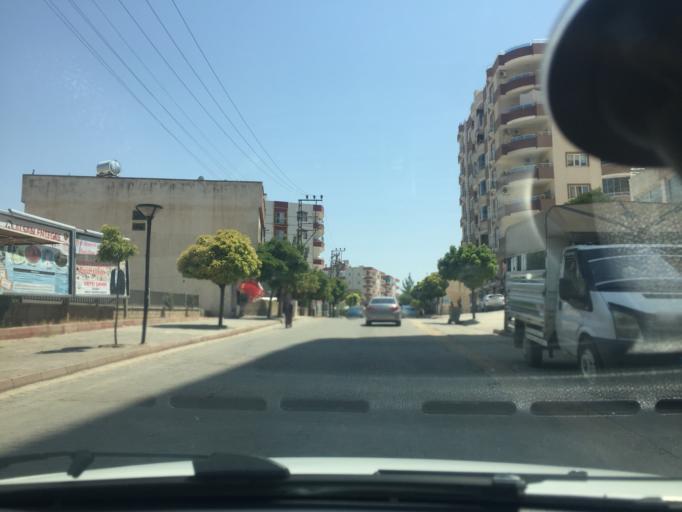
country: TR
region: Mardin
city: Midyat
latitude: 37.4301
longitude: 41.3375
